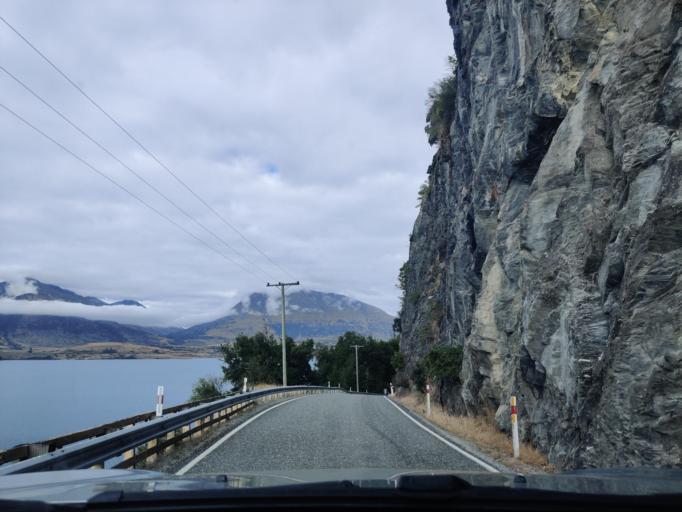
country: NZ
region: Otago
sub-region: Queenstown-Lakes District
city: Queenstown
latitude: -45.0785
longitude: 168.4866
